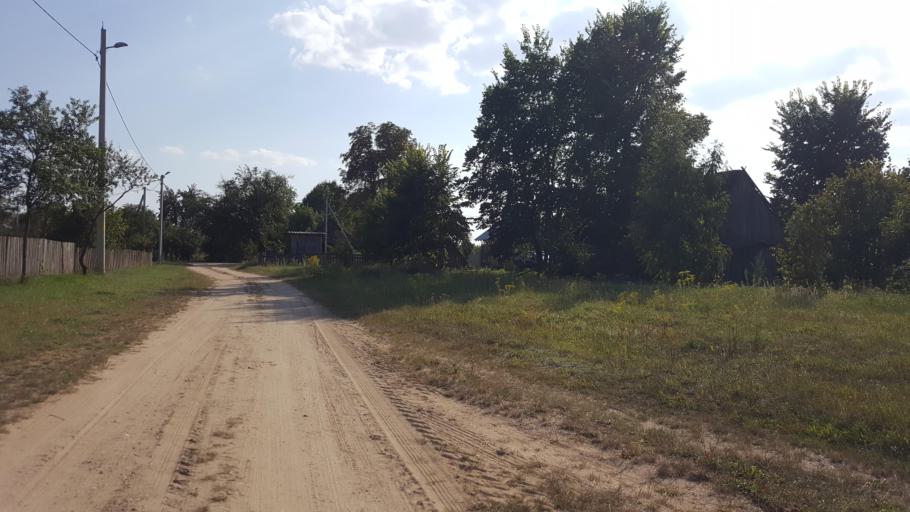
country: BY
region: Brest
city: Kamyanyuki
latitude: 52.5620
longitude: 23.6405
